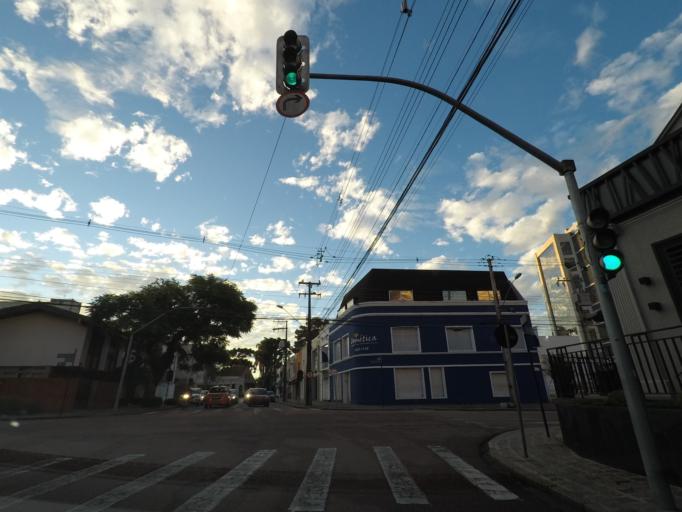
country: BR
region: Parana
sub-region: Curitiba
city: Curitiba
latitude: -25.4456
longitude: -49.2930
